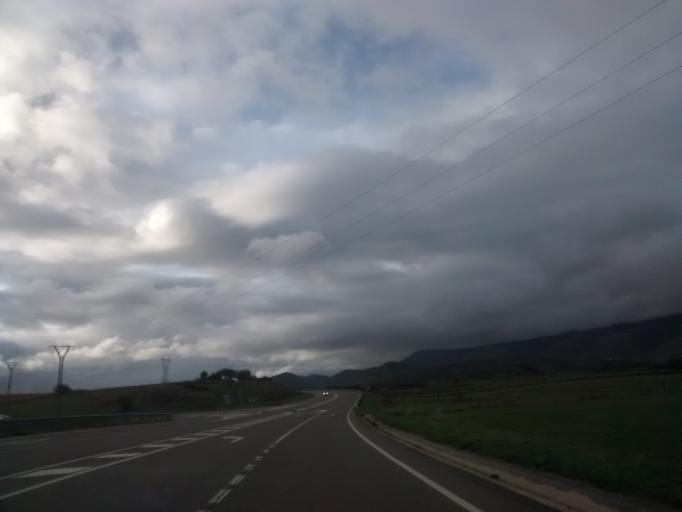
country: ES
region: Cantabria
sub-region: Provincia de Cantabria
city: Reinosa
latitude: 43.0056
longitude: -4.1029
